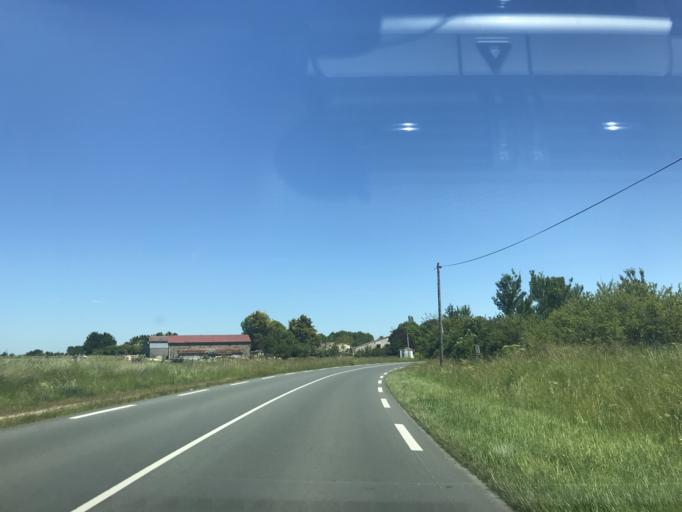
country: FR
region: Poitou-Charentes
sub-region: Departement de la Charente-Maritime
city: Meschers-sur-Gironde
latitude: 45.5621
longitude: -0.9397
